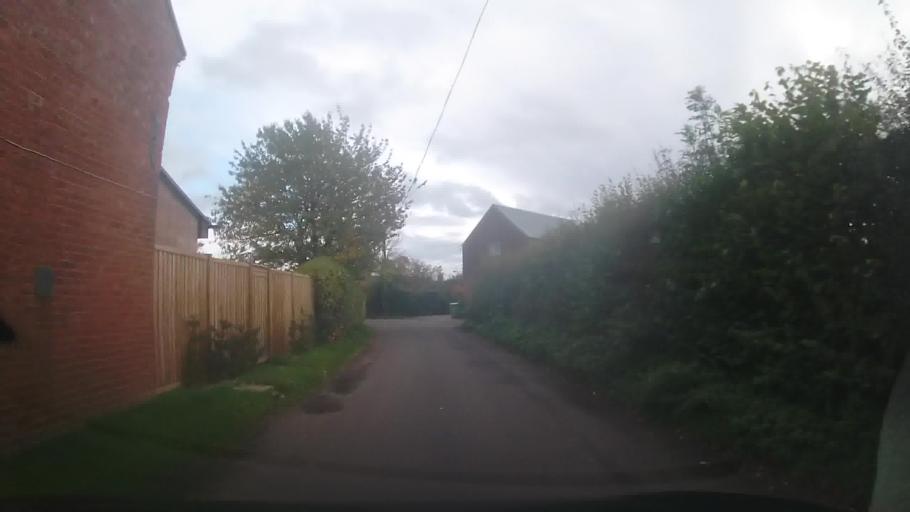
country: GB
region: England
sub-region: Shropshire
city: Wem
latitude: 52.8695
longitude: -2.7224
